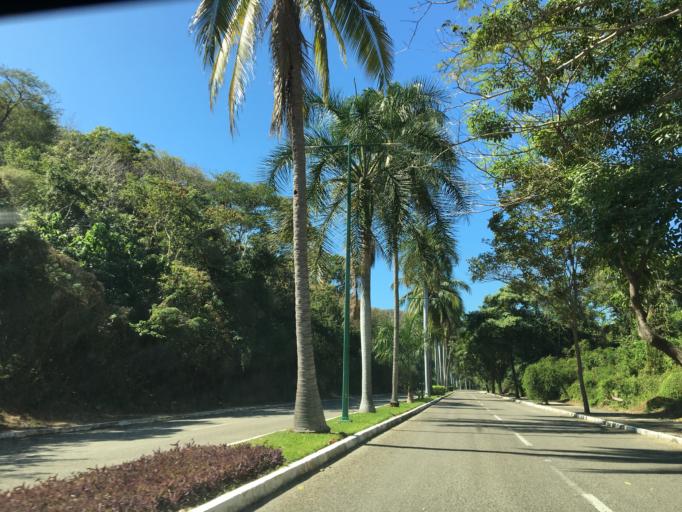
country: MX
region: Oaxaca
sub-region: Santa Maria Huatulco
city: Crucecita
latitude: 15.7816
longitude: -96.1099
